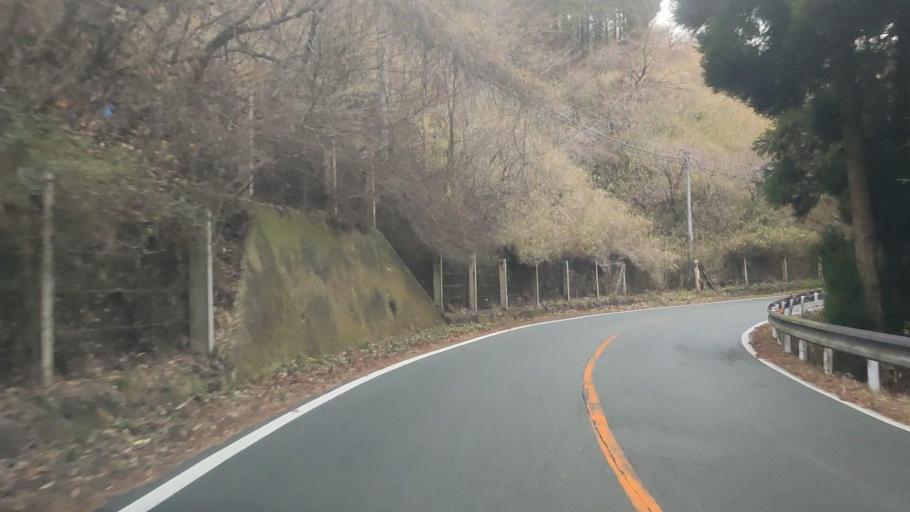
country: JP
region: Kumamoto
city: Aso
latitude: 32.8780
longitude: 131.1705
